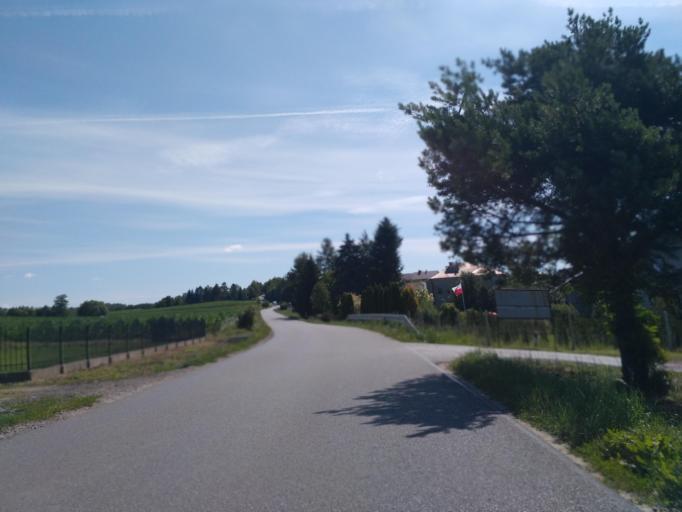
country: PL
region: Subcarpathian Voivodeship
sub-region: Powiat krosnienski
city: Kroscienko Wyzne
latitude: 49.7051
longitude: 21.8400
